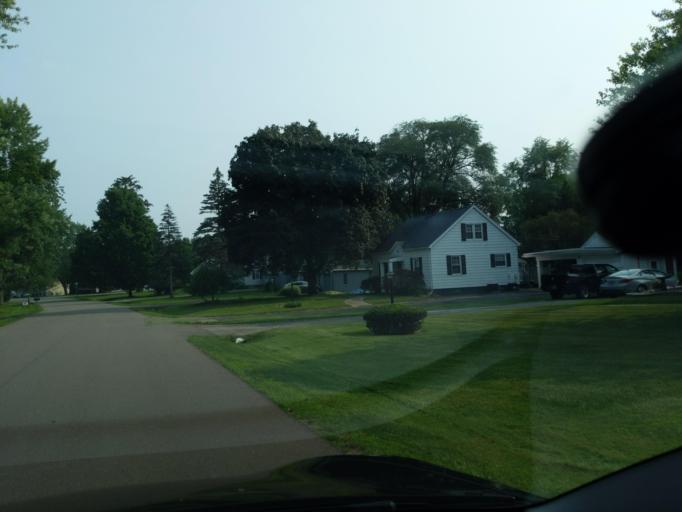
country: US
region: Michigan
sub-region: Jackson County
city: Jackson
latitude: 42.2367
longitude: -84.4457
